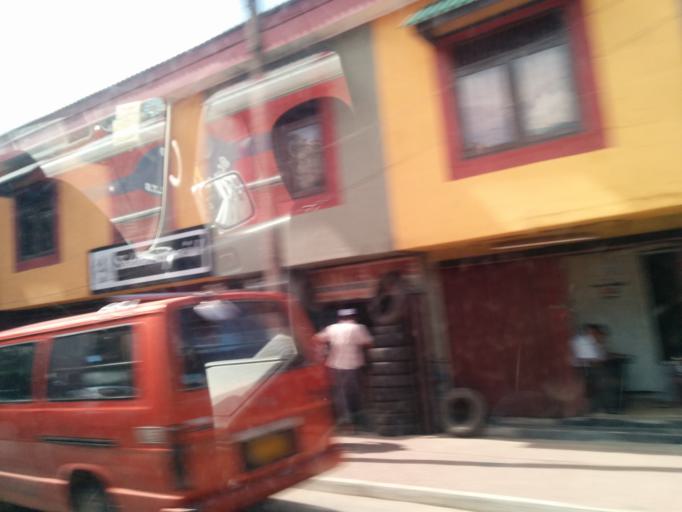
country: LK
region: Western
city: Colombo
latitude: 6.9330
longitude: 79.8634
